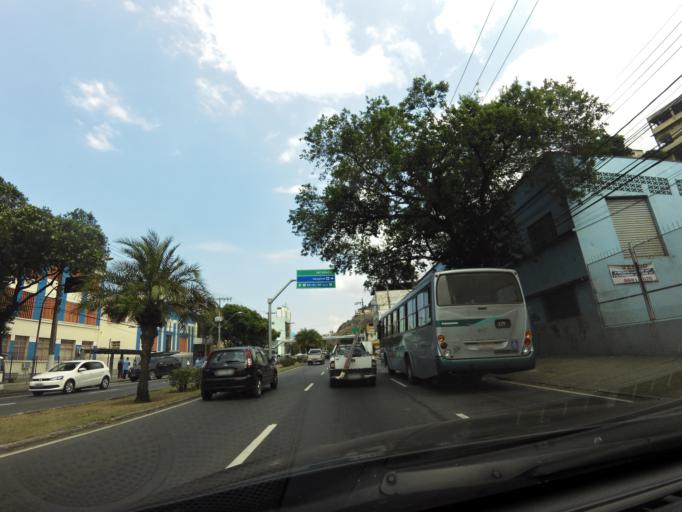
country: BR
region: Espirito Santo
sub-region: Vitoria
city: Vitoria
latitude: -20.3164
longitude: -40.3236
